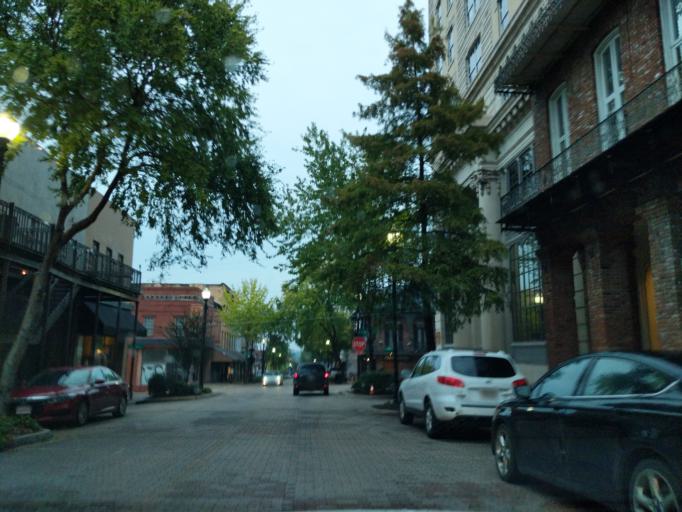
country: US
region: Mississippi
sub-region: Warren County
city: Vicksburg
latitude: 32.3497
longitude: -90.8822
